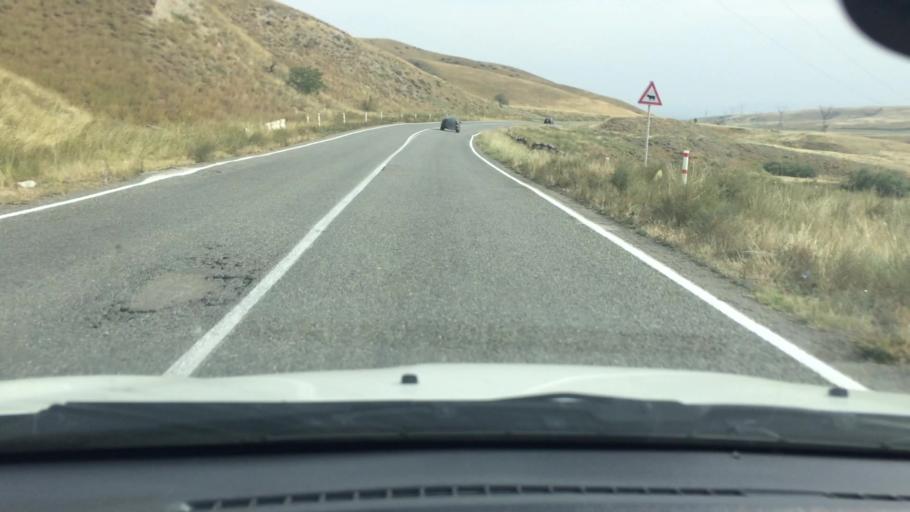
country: GE
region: Kvemo Kartli
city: Rust'avi
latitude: 41.5068
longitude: 44.9519
